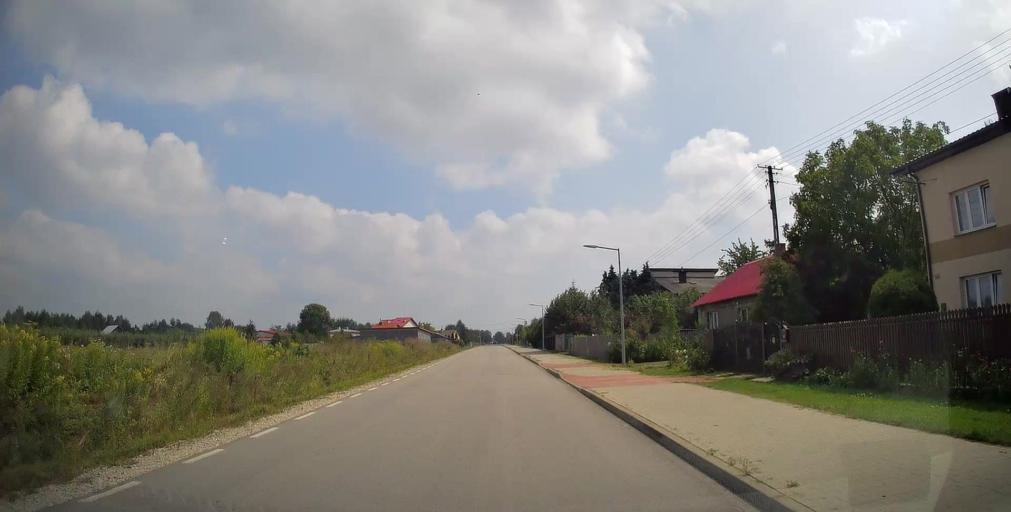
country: PL
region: Masovian Voivodeship
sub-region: Powiat bialobrzeski
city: Sucha
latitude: 51.6117
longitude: 20.9700
